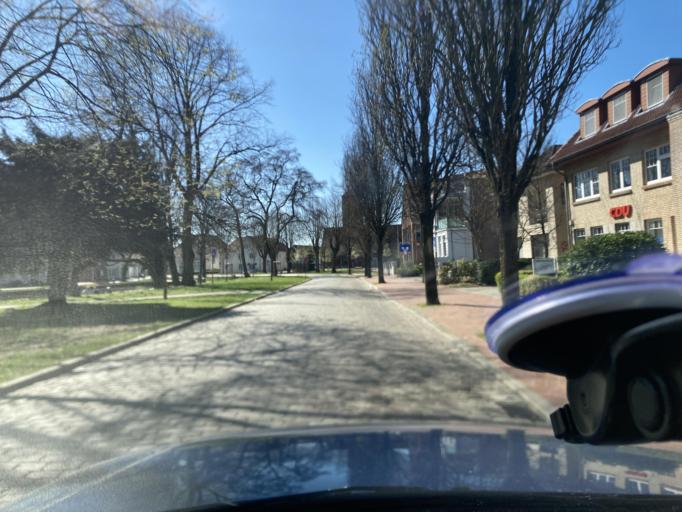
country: DE
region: Schleswig-Holstein
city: Heide
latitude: 54.1931
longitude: 9.0943
